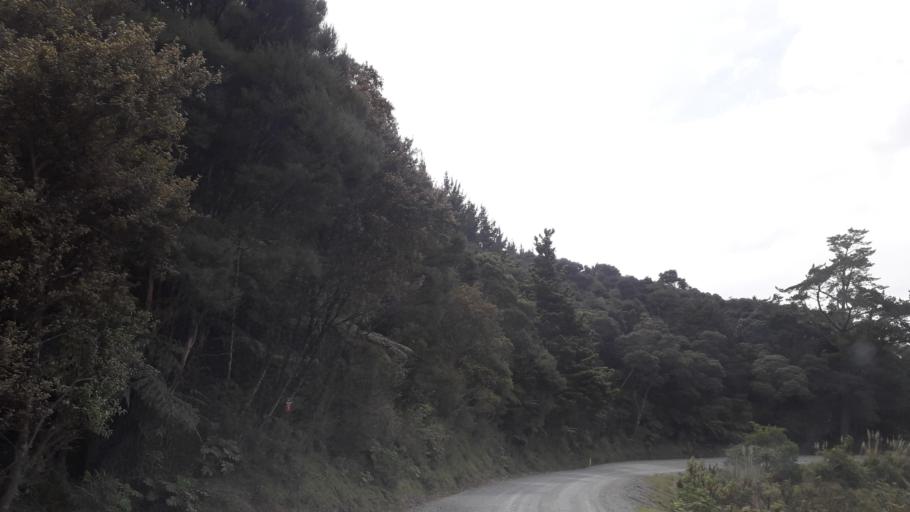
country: NZ
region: Northland
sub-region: Far North District
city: Taipa
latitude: -35.0409
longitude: 173.5643
